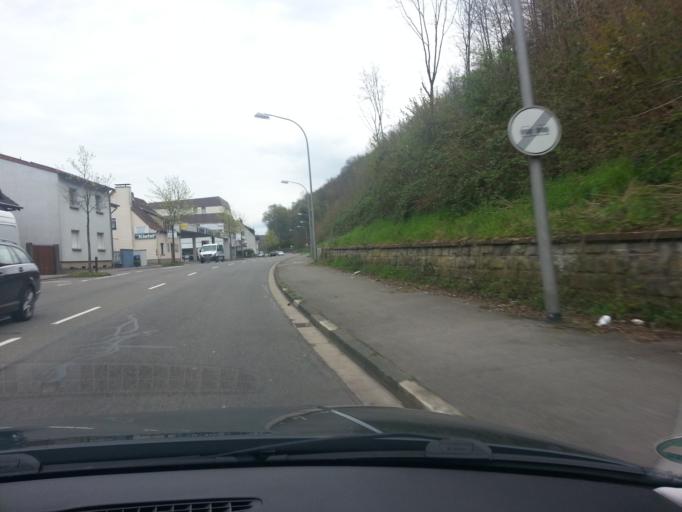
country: DE
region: Saarland
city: Sulzbach
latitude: 49.2353
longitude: 7.0550
